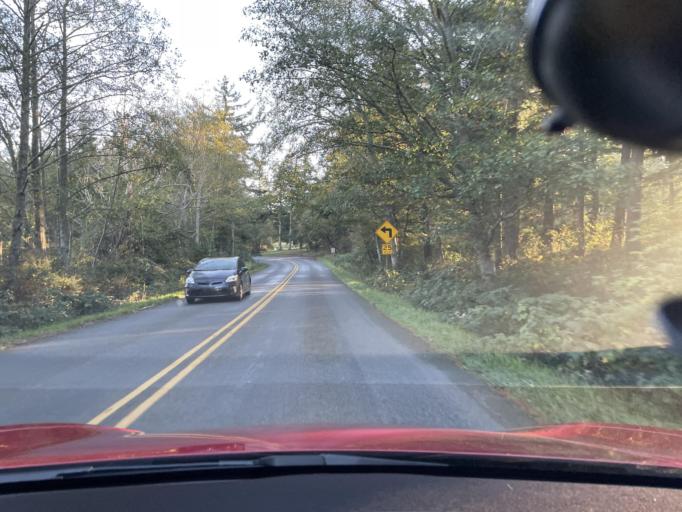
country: US
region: Washington
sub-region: San Juan County
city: Friday Harbor
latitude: 48.5628
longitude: -123.1539
